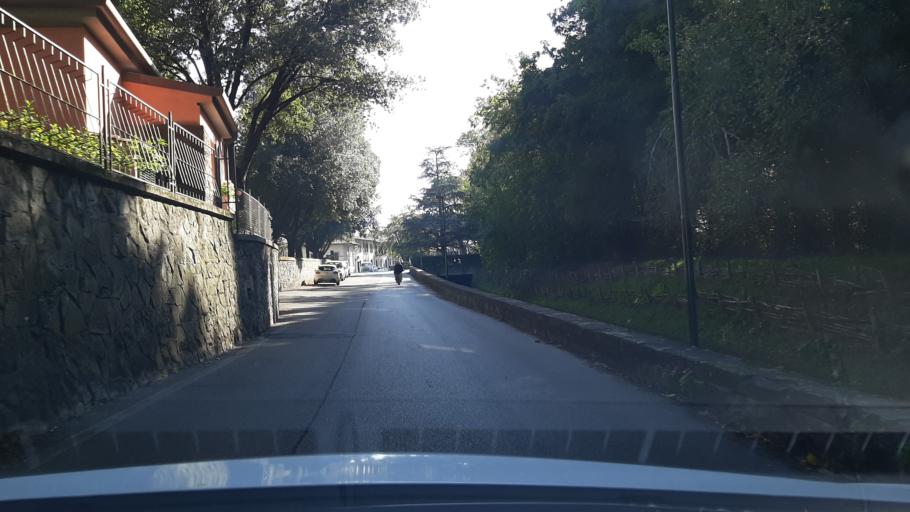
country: IT
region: Tuscany
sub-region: Province of Florence
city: Fiesole
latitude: 43.7864
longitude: 11.2942
